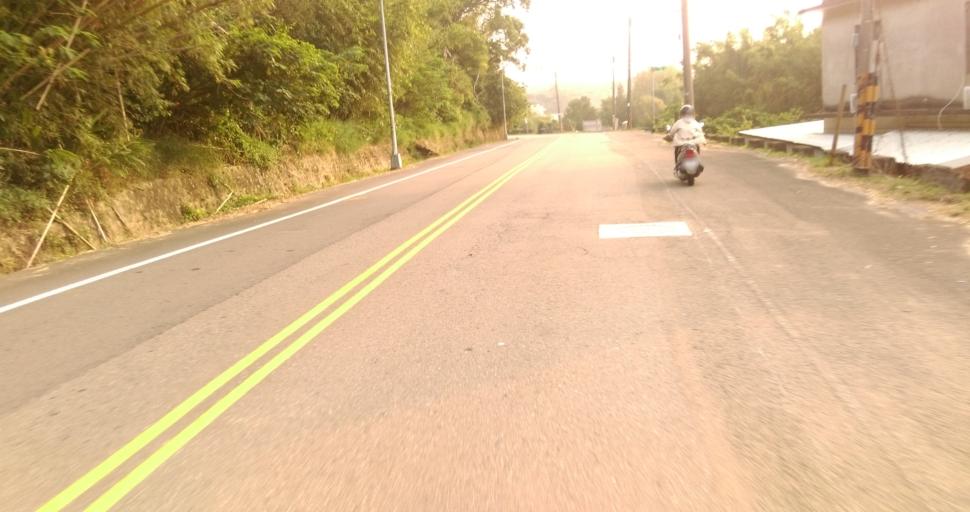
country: TW
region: Taiwan
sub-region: Hsinchu
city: Hsinchu
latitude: 24.7501
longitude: 120.9378
